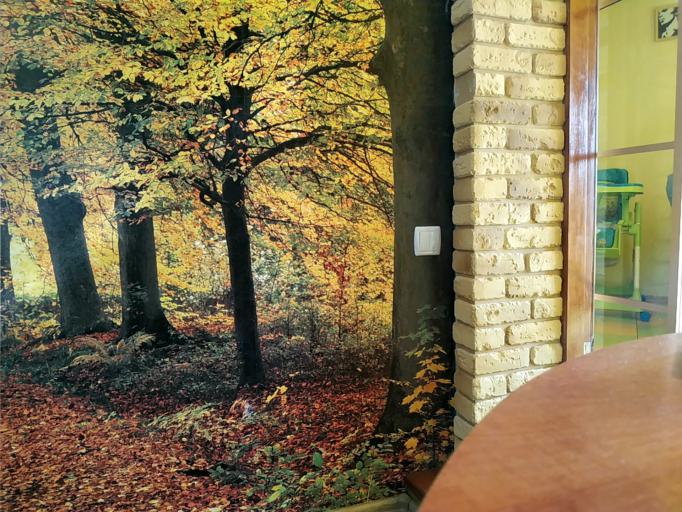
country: RU
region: Novgorod
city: Parfino
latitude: 57.8069
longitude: 31.5868
